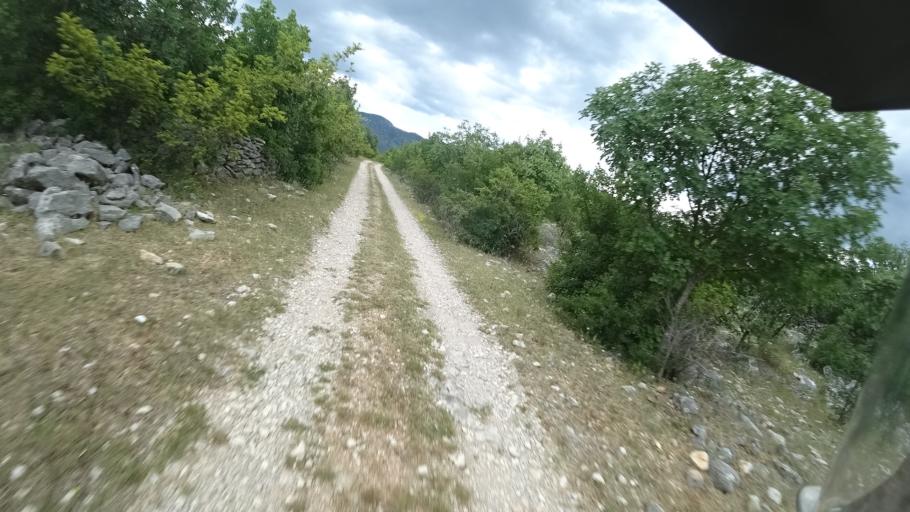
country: HR
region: Zadarska
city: Gracac
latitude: 44.1559
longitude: 15.9356
